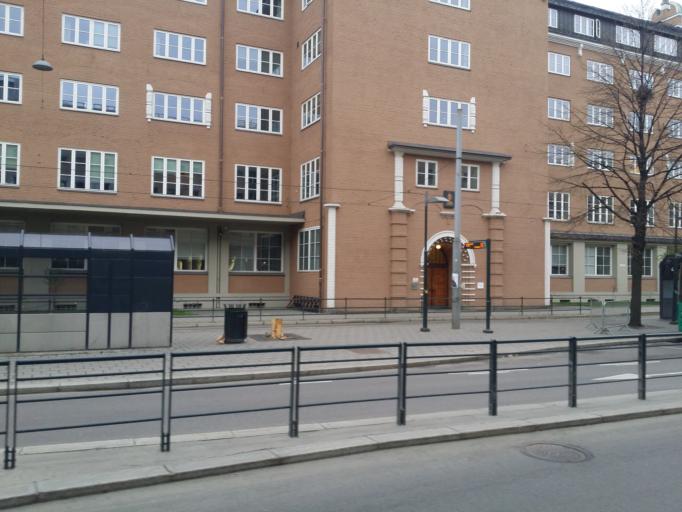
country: NO
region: Oslo
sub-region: Oslo
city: Oslo
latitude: 59.9111
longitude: 10.7594
